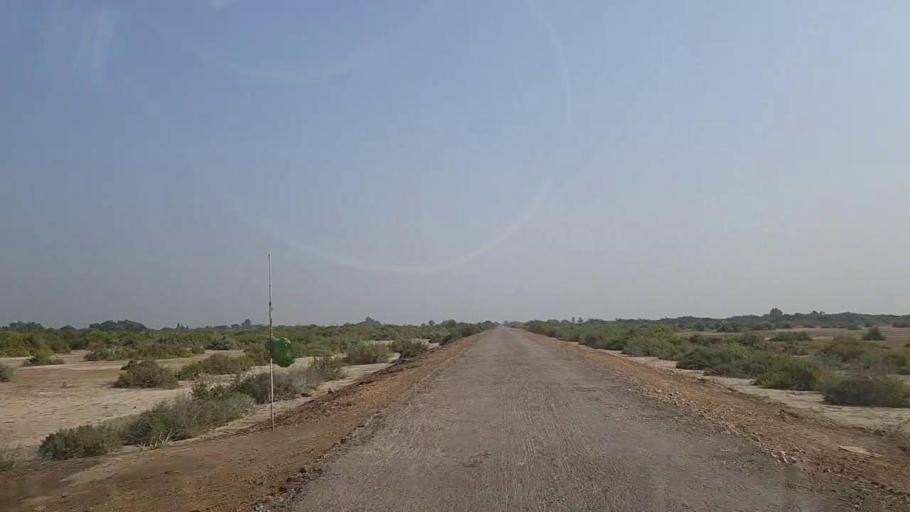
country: PK
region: Sindh
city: Keti Bandar
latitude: 24.2307
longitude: 67.6540
